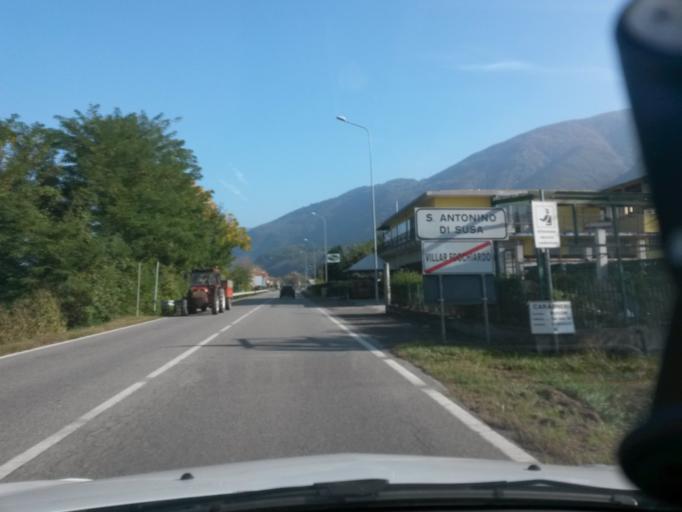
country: IT
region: Piedmont
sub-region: Provincia di Torino
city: Villar Focchiardo
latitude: 45.1098
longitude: 7.2554
